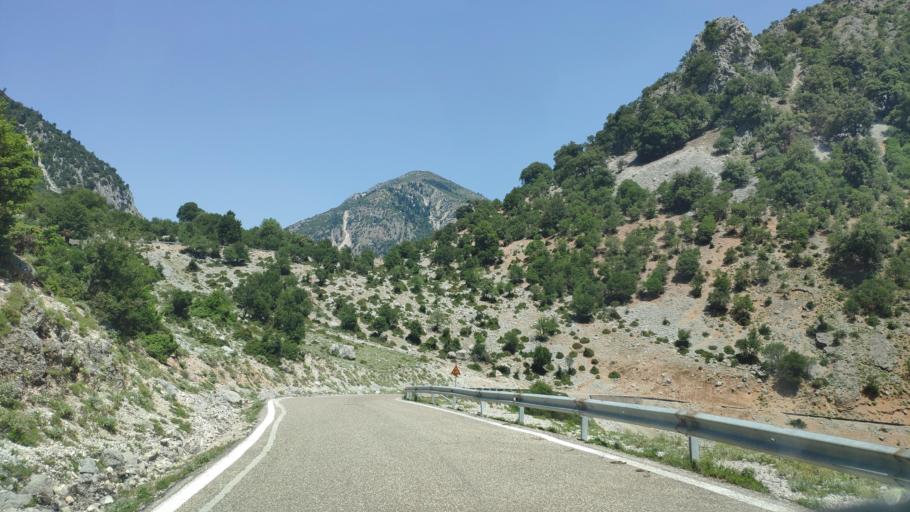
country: GR
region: West Greece
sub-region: Nomos Aitolias kai Akarnanias
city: Krikellos
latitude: 39.0075
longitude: 21.3620
